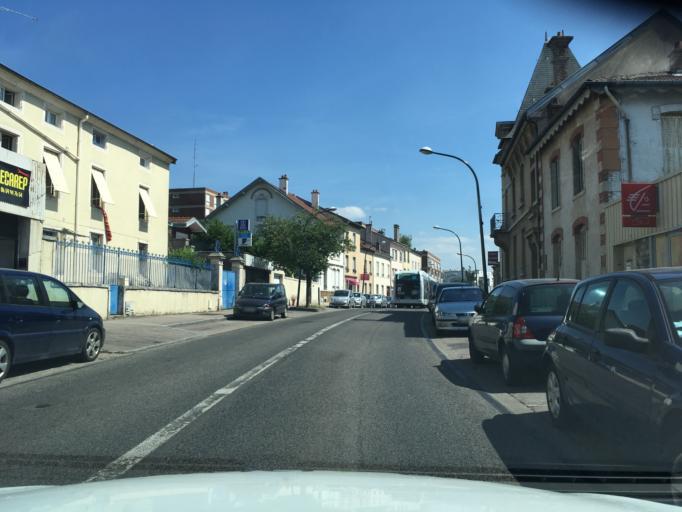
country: FR
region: Lorraine
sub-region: Departement de Meurthe-et-Moselle
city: Jarville-la-Malgrange
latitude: 48.6748
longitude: 6.2012
